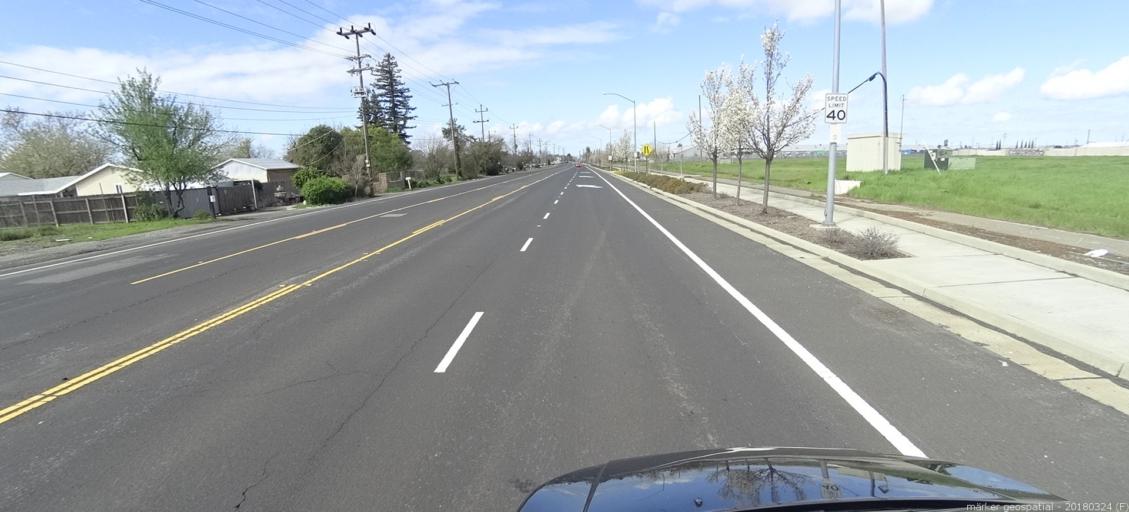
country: US
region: California
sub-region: Sacramento County
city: North Highlands
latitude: 38.6472
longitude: -121.4118
